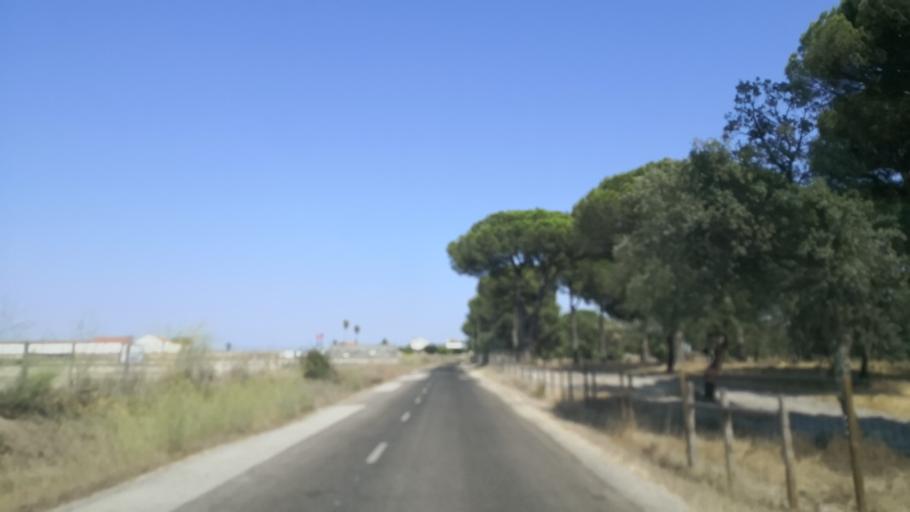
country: PT
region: Santarem
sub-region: Benavente
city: Poceirao
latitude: 38.7450
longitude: -8.6783
